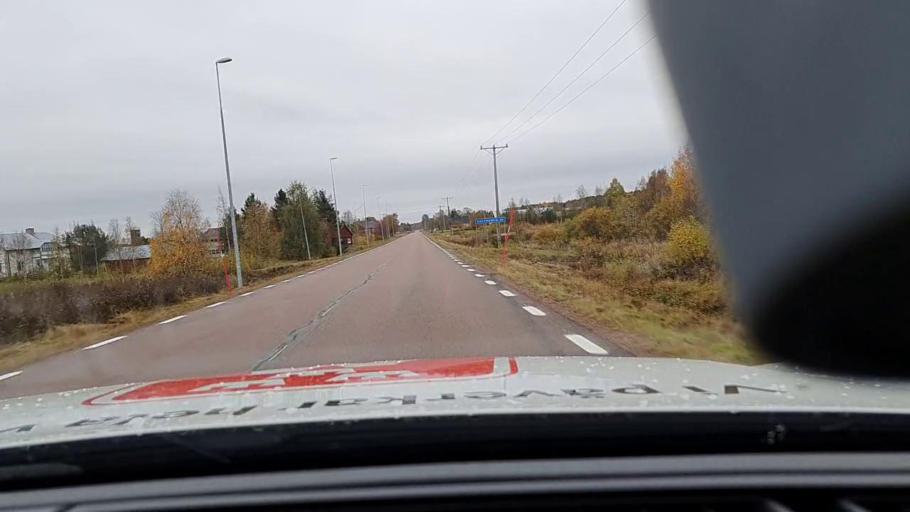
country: FI
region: Lapland
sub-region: Torniolaakso
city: Ylitornio
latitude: 66.1387
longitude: 23.9014
